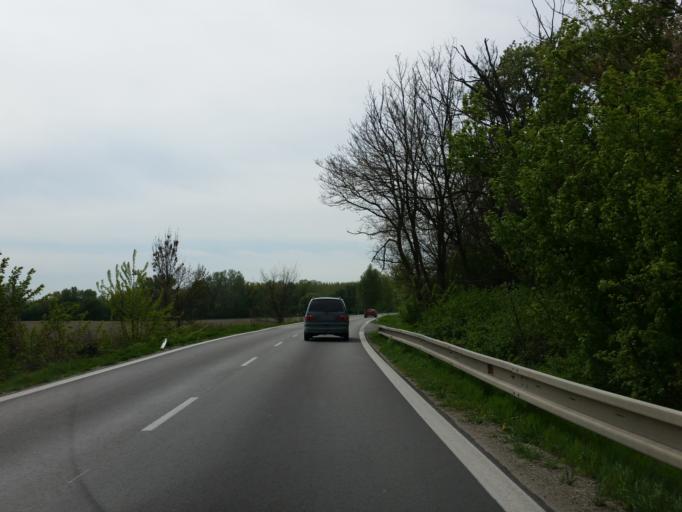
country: SK
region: Trnavsky
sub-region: Okres Dunajska Streda
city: Velky Meder
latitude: 47.9974
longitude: 17.8059
